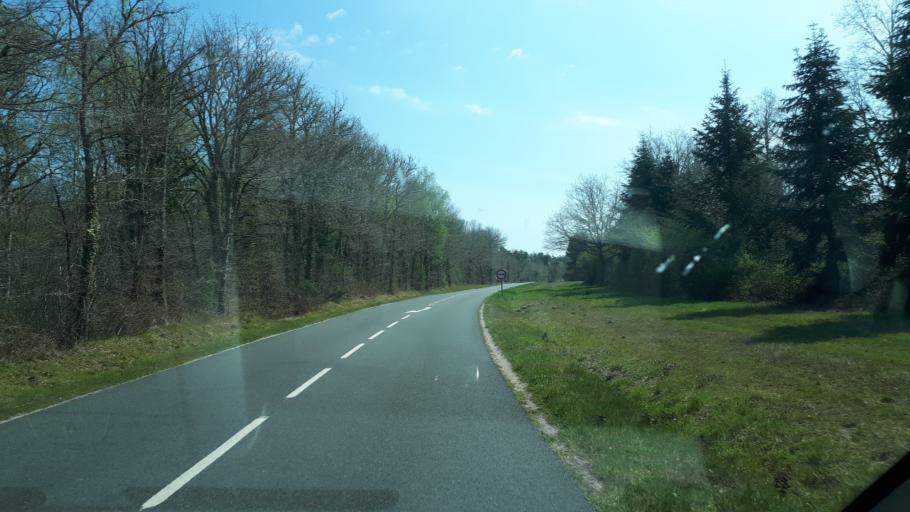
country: FR
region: Centre
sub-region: Departement du Loir-et-Cher
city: Selles-Saint-Denis
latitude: 47.3385
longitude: 1.9234
